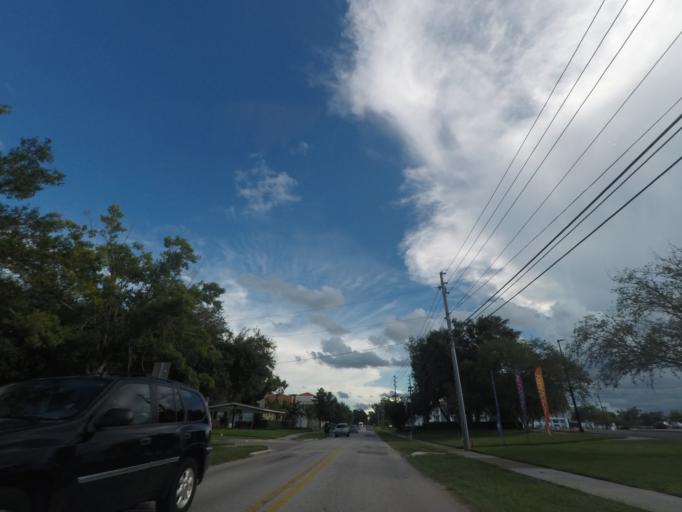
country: US
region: Florida
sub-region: Orange County
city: Fairview Shores
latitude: 28.5880
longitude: -81.3733
